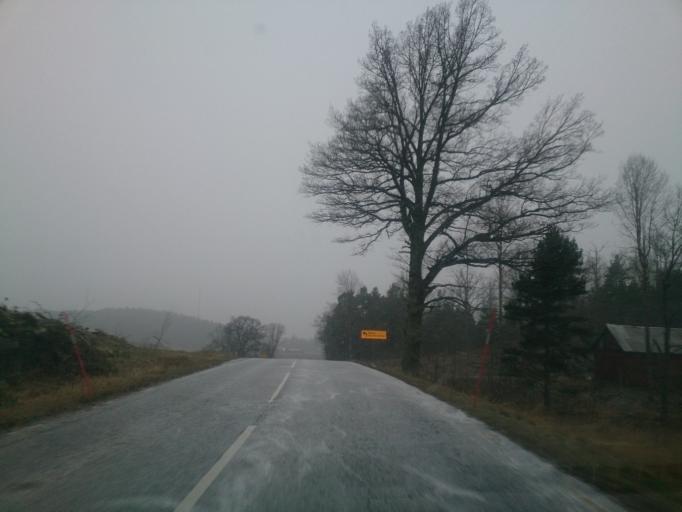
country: SE
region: OEstergoetland
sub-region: Soderkopings Kommun
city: Soederkoeping
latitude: 58.5024
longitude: 16.3188
